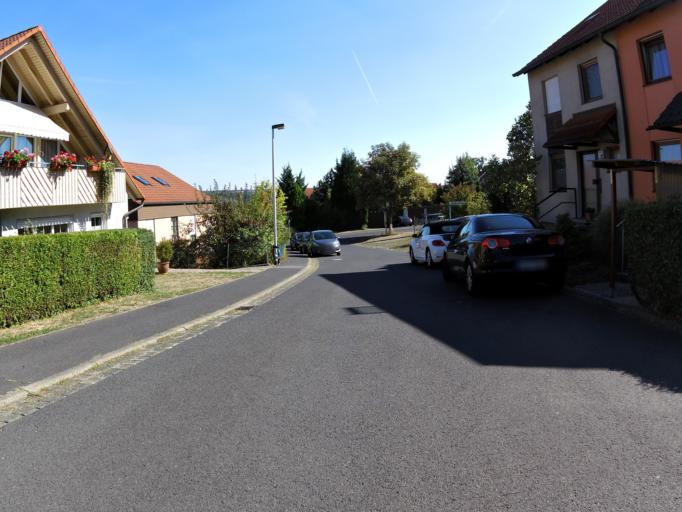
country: DE
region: Bavaria
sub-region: Regierungsbezirk Unterfranken
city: Margetshochheim
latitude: 49.8411
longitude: 9.8571
